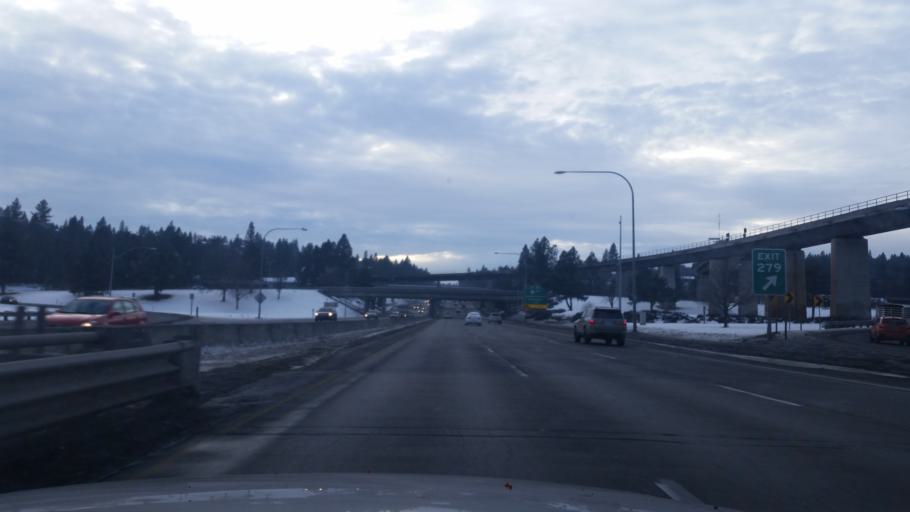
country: US
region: Washington
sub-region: Spokane County
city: Spokane
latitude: 47.6478
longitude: -117.4489
